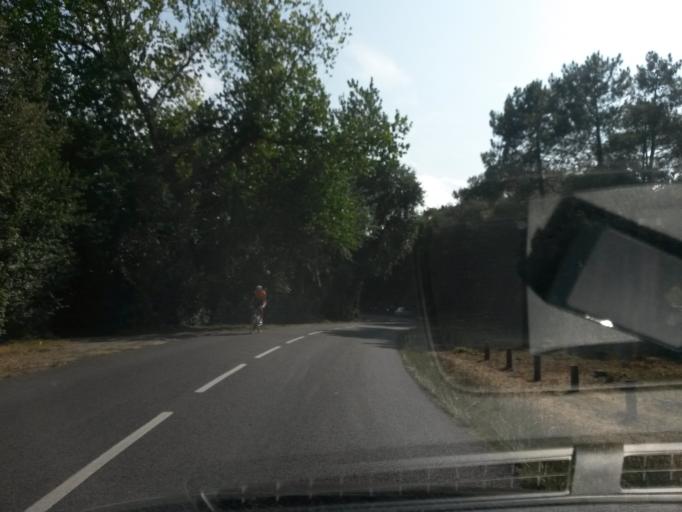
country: FR
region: Pays de la Loire
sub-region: Departement de la Vendee
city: Olonne-sur-Mer
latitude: 46.5353
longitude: -1.8129
